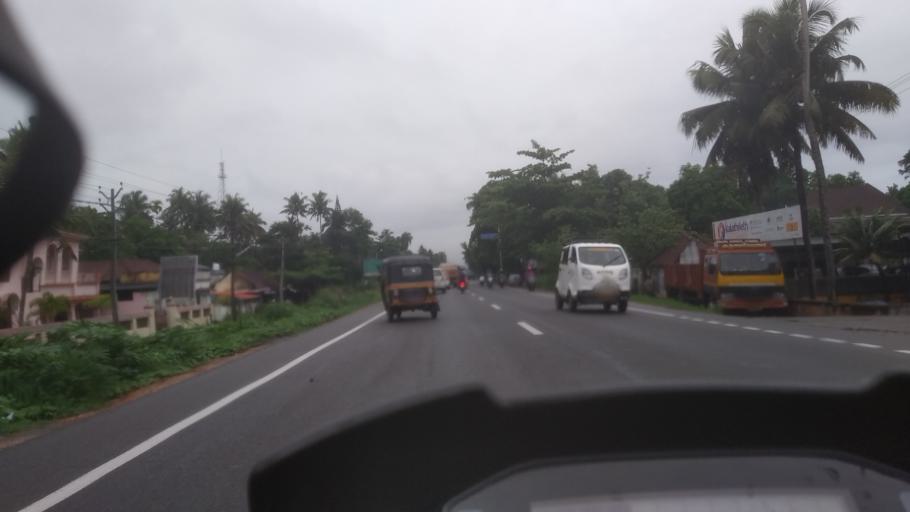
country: IN
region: Kerala
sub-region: Alappuzha
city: Kayankulam
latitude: 9.1647
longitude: 76.5027
